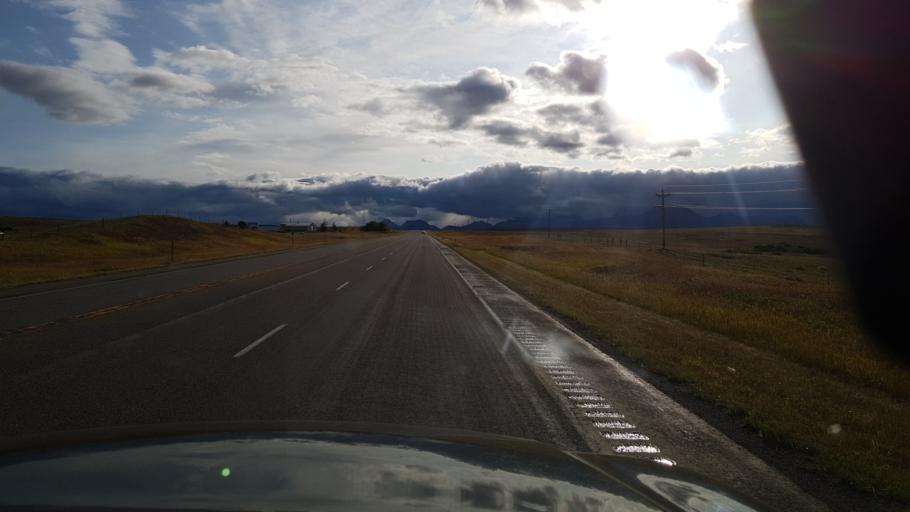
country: US
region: Montana
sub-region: Glacier County
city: South Browning
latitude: 48.5113
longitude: -113.0932
